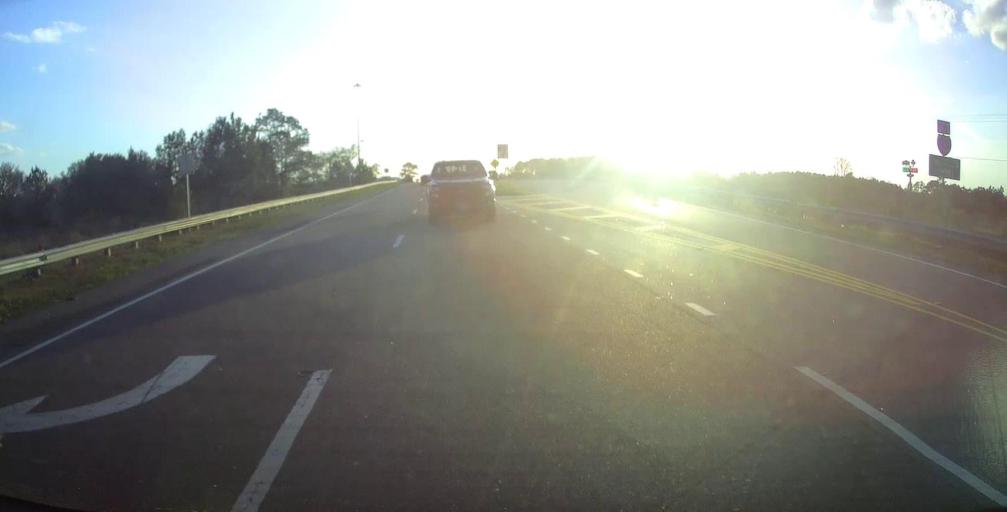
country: US
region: Georgia
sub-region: Chatham County
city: Bloomingdale
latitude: 32.1825
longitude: -81.4572
